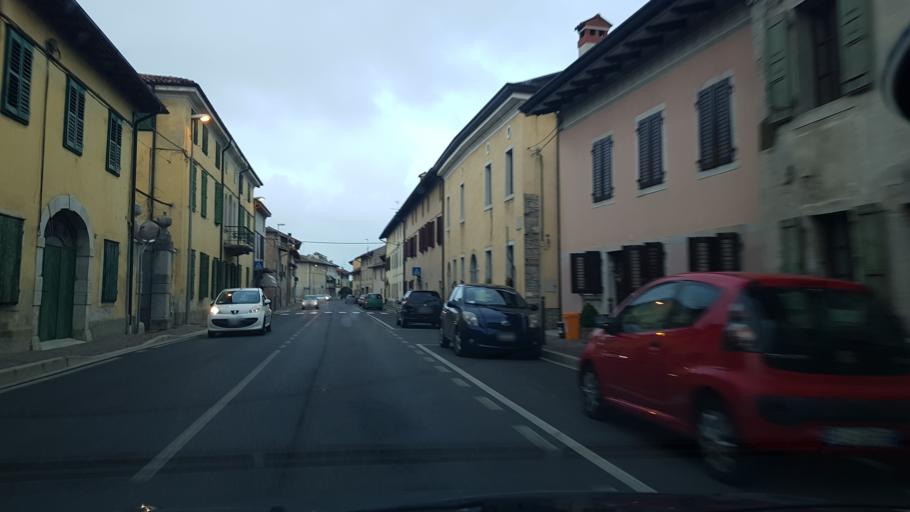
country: IT
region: Friuli Venezia Giulia
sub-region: Provincia di Gorizia
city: Medea
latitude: 45.9000
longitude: 13.4164
